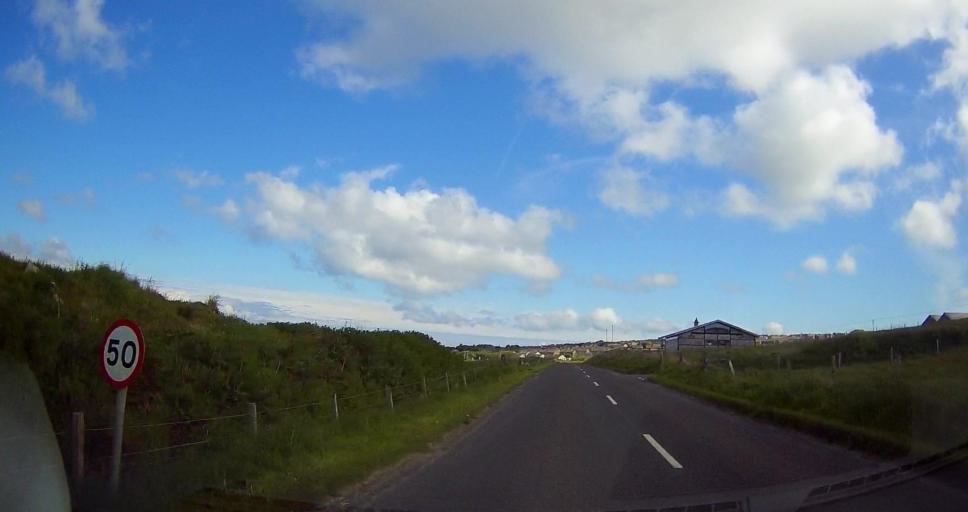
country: GB
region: Scotland
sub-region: Orkney Islands
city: Orkney
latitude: 58.9689
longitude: -2.9632
